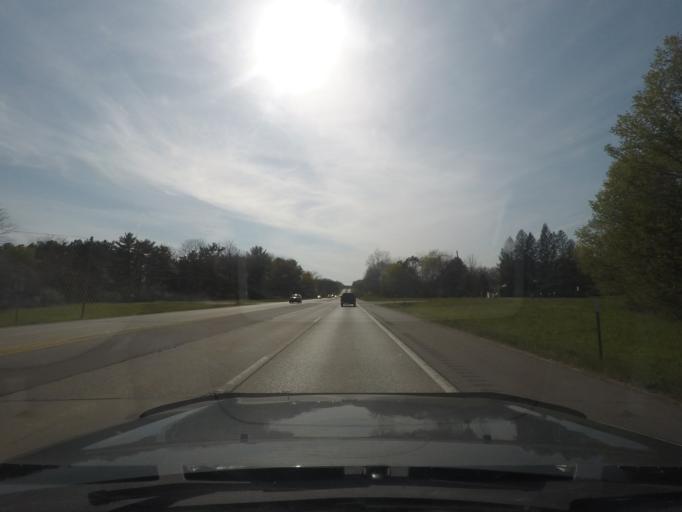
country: US
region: Michigan
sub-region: Berrien County
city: Niles
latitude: 41.8013
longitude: -86.2625
